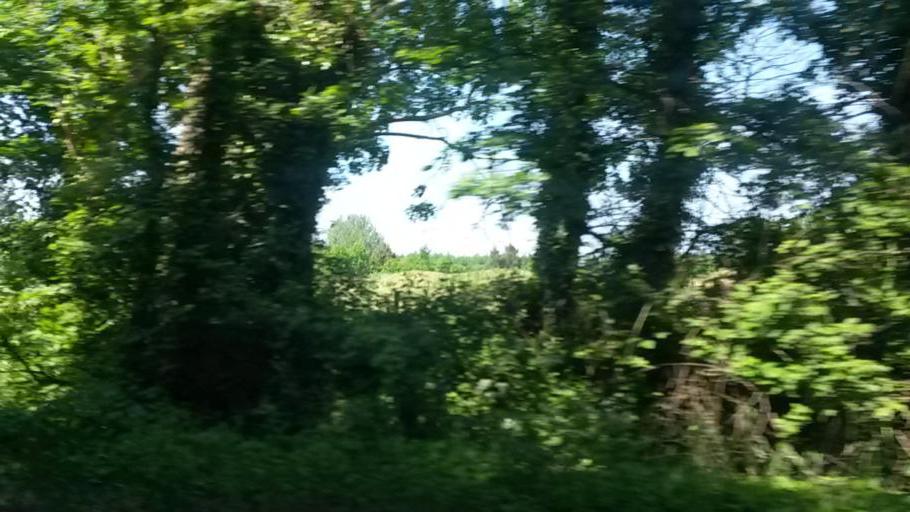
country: IE
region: Leinster
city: Donabate
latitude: 53.4894
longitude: -6.1673
